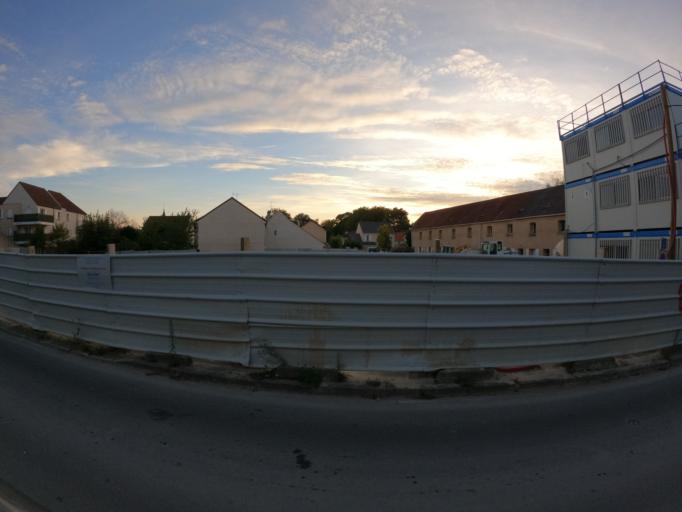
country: FR
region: Ile-de-France
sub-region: Departement de Seine-et-Marne
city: Emerainville
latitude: 48.8132
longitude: 2.6222
